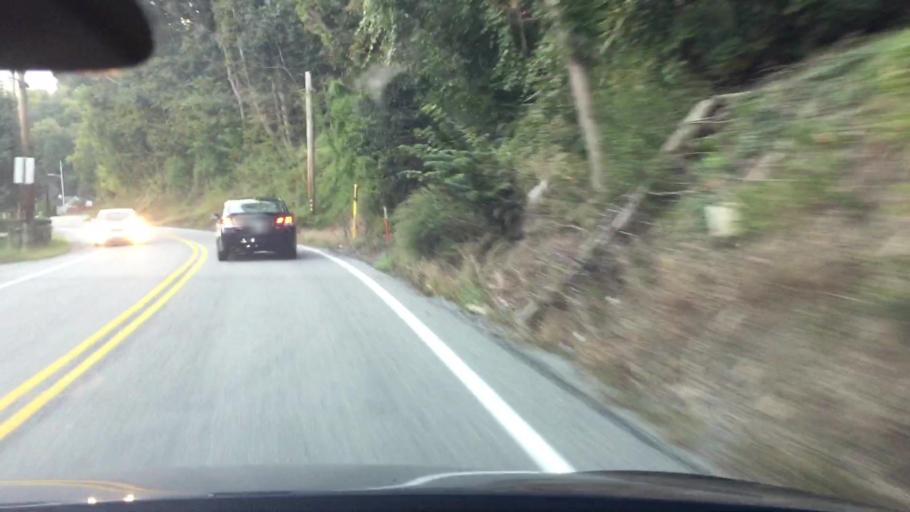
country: US
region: Pennsylvania
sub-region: Allegheny County
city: Etna
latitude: 40.5204
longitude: -79.9383
